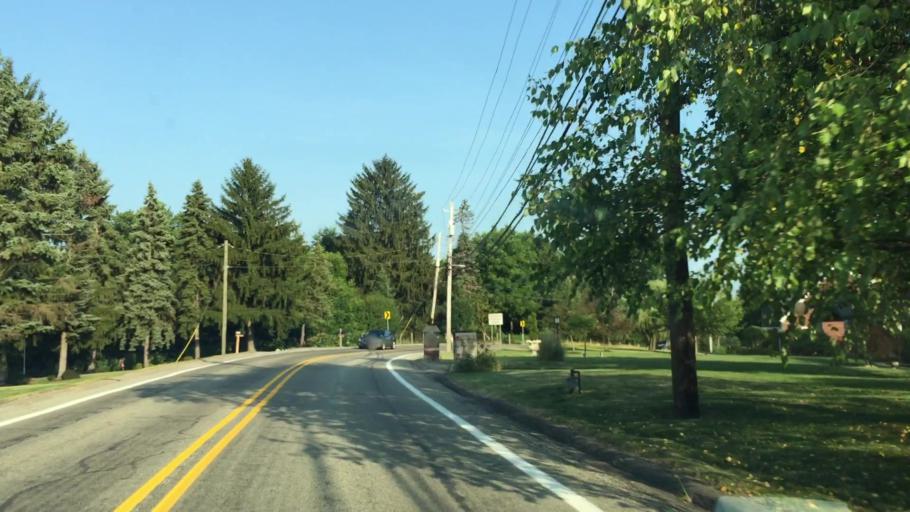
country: US
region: Pennsylvania
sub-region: Allegheny County
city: Bridgeville
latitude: 40.3313
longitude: -80.1268
